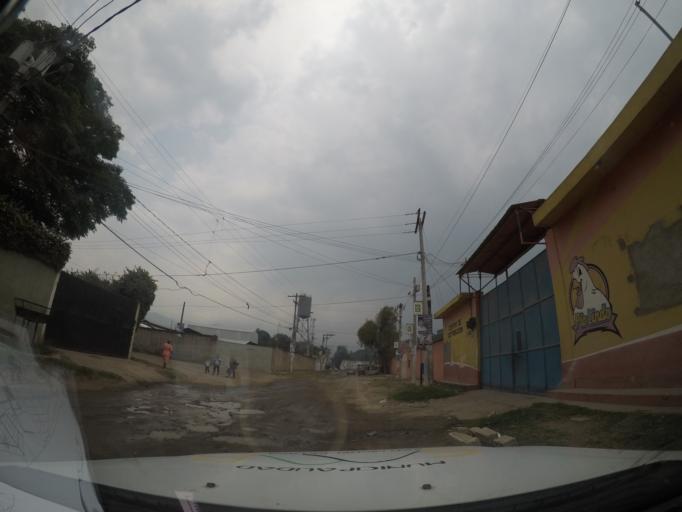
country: GT
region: Guatemala
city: Petapa
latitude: 14.5089
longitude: -90.5545
